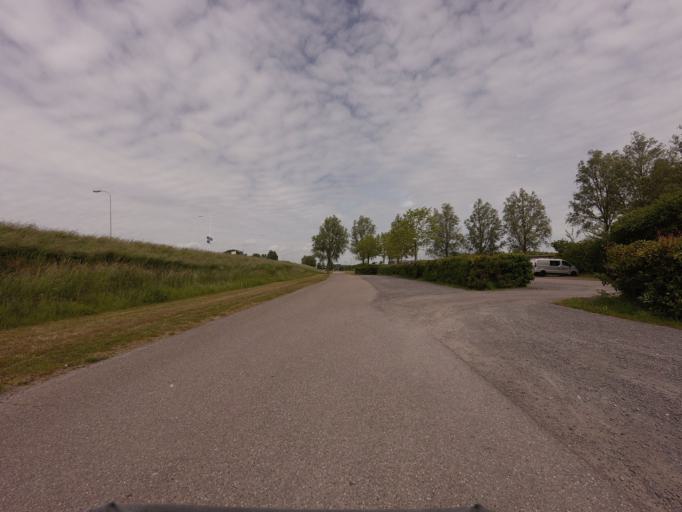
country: NL
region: North Holland
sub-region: Gemeente Medemblik
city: Medemblik
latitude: 52.7660
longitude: 5.1173
